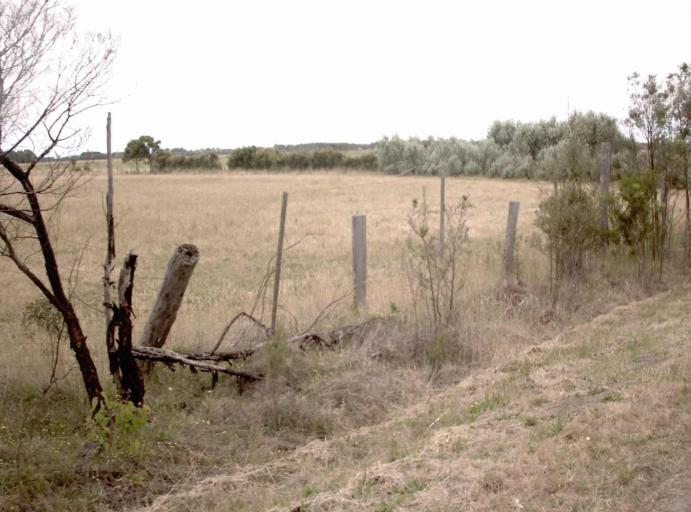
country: AU
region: Victoria
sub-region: Latrobe
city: Traralgon
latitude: -38.4805
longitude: 146.8211
